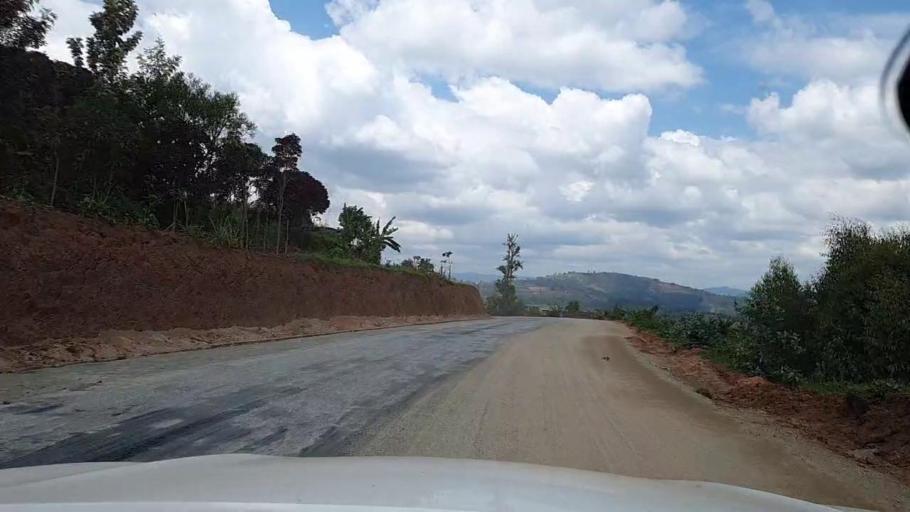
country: RW
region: Southern Province
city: Butare
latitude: -2.6985
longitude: 29.5650
